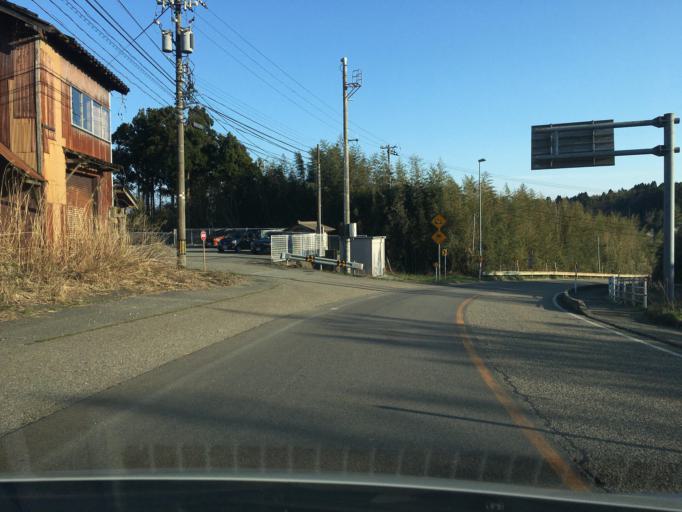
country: JP
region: Ishikawa
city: Nanao
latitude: 36.9801
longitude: 137.0503
